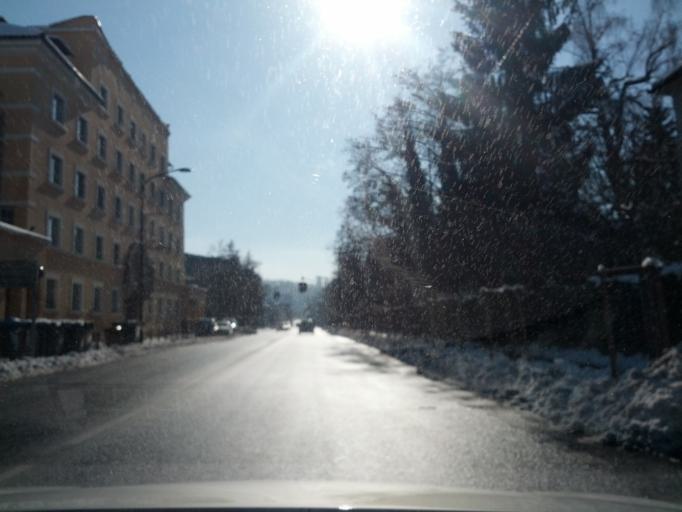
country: SI
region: Ljubljana
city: Ljubljana
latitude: 46.0548
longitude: 14.5190
